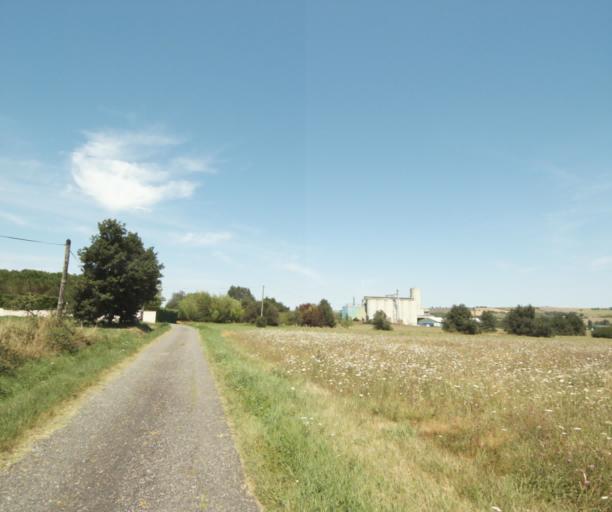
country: FR
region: Midi-Pyrenees
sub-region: Departement de l'Ariege
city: Lezat-sur-Leze
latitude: 43.2865
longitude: 1.3392
